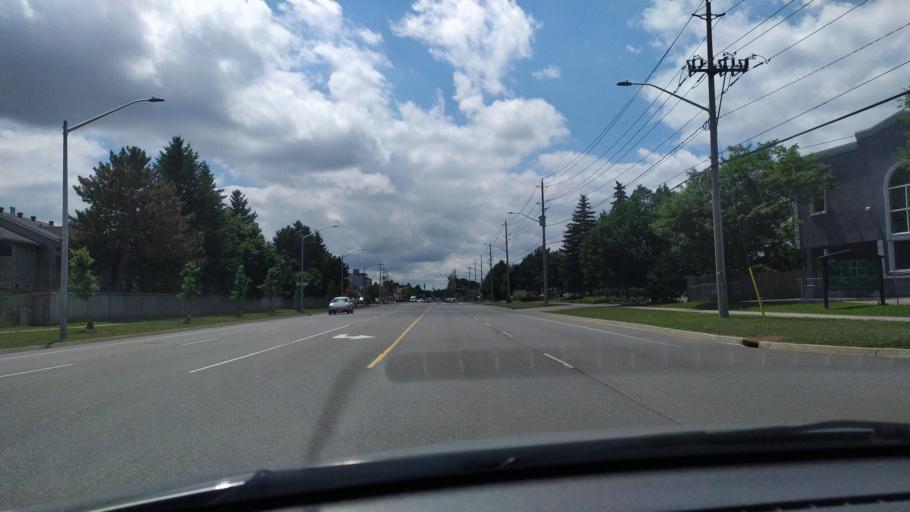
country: CA
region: Ontario
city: Kitchener
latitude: 43.4520
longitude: -80.4413
